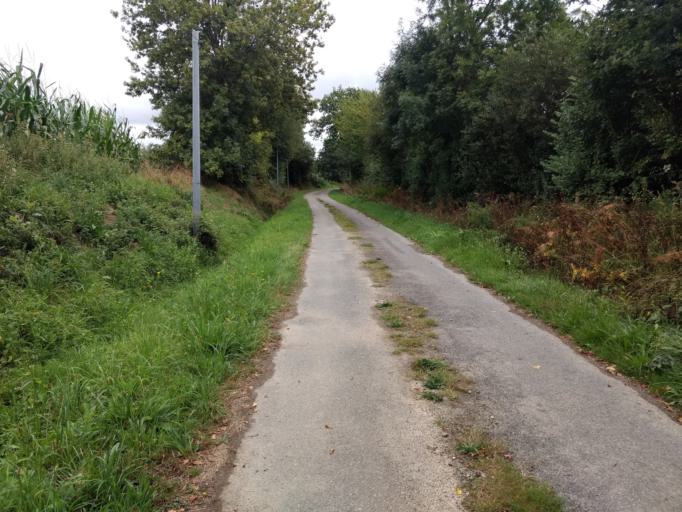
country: FR
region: Brittany
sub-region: Departement du Finistere
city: Loperhet
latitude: 48.3576
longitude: -4.2940
